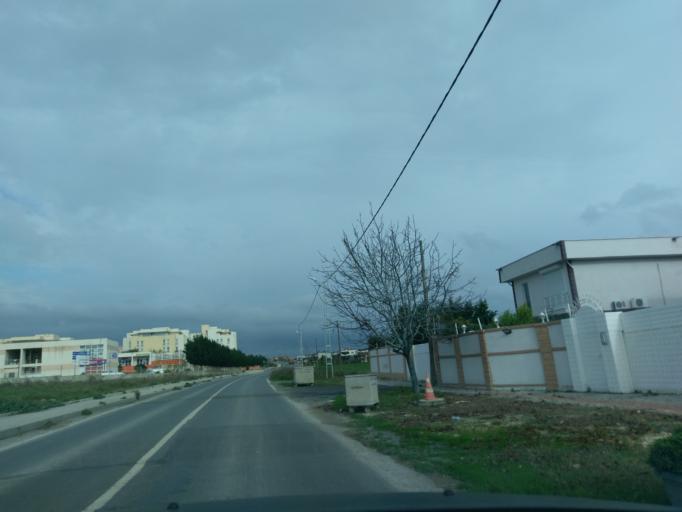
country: TR
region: Istanbul
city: Selimpasa
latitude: 41.0744
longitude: 28.3708
